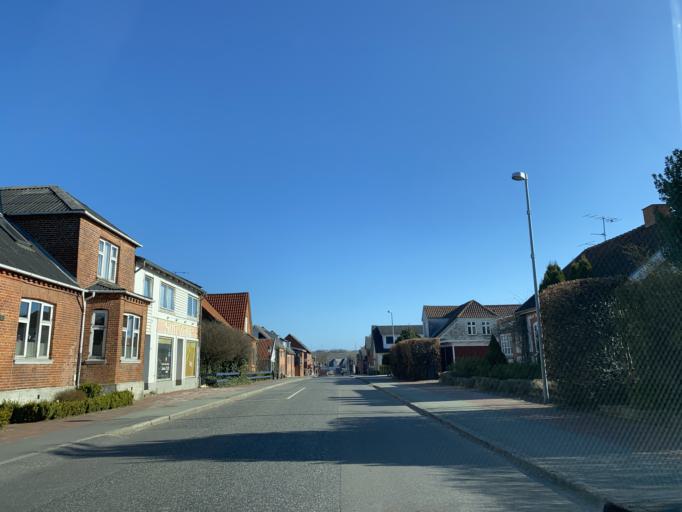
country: DK
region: Central Jutland
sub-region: Favrskov Kommune
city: Ulstrup
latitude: 56.3893
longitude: 9.7916
